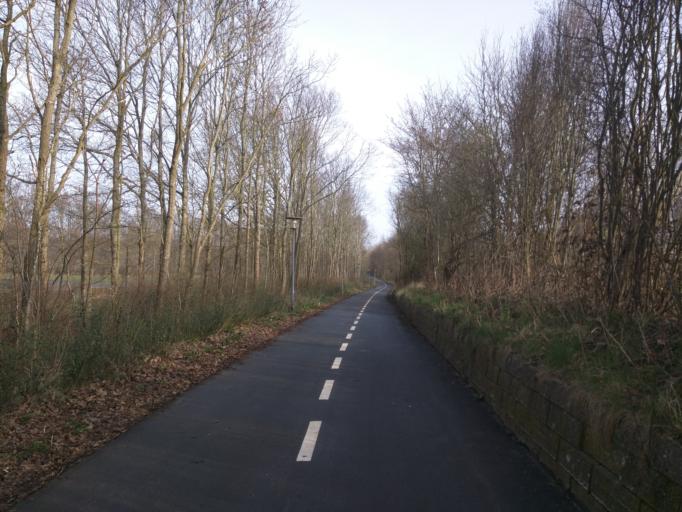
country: DK
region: South Denmark
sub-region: Fredericia Kommune
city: Snoghoj
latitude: 55.5406
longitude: 9.7070
